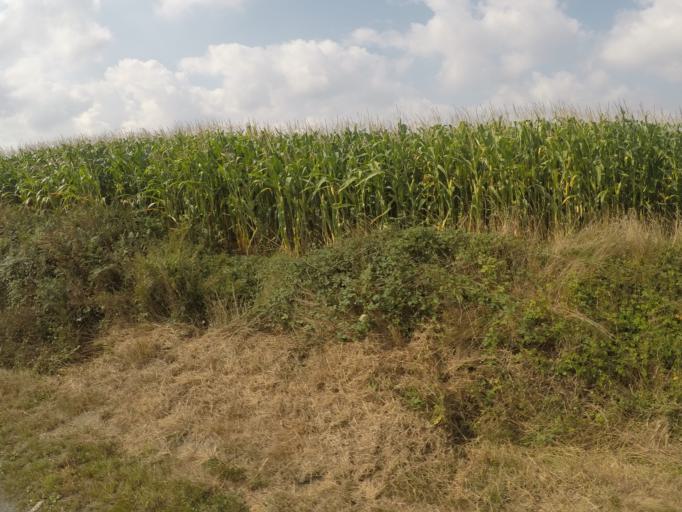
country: FR
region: Brittany
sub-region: Departement des Cotes-d'Armor
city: Saint-Donan
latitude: 48.5110
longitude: -2.9141
